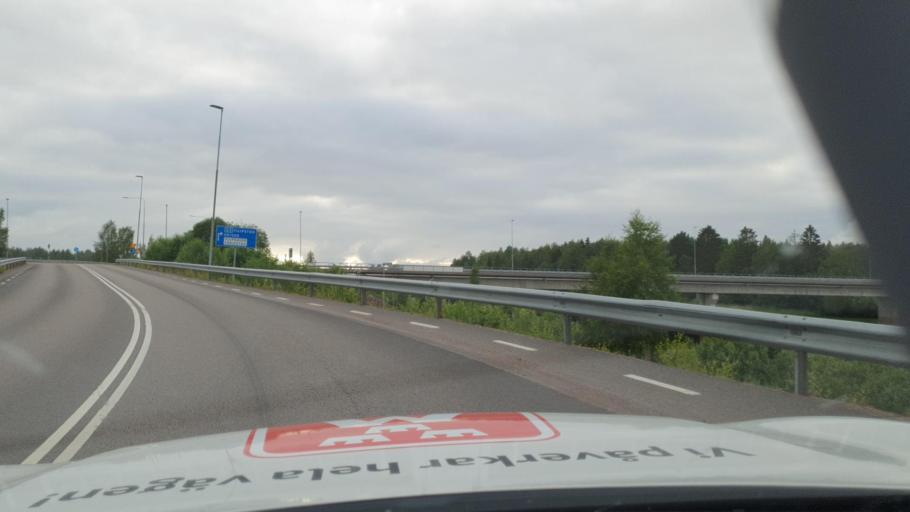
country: SE
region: Vaermland
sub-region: Karlstads Kommun
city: Karlstad
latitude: 59.4272
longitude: 13.4562
